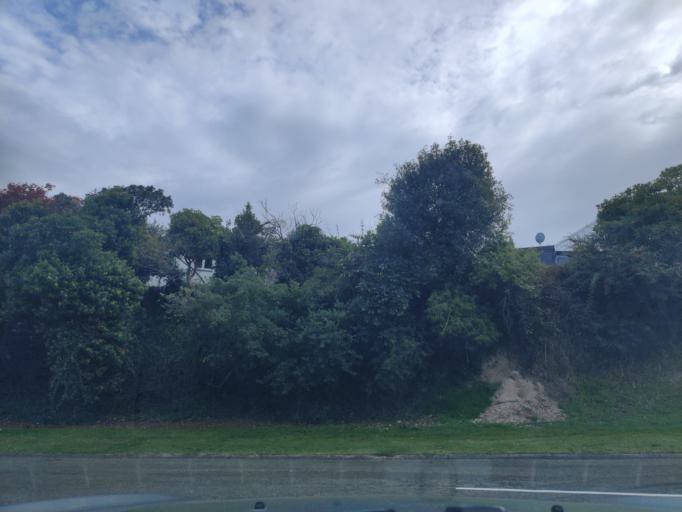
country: NZ
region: Waikato
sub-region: Taupo District
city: Taupo
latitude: -38.7101
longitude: 176.0937
